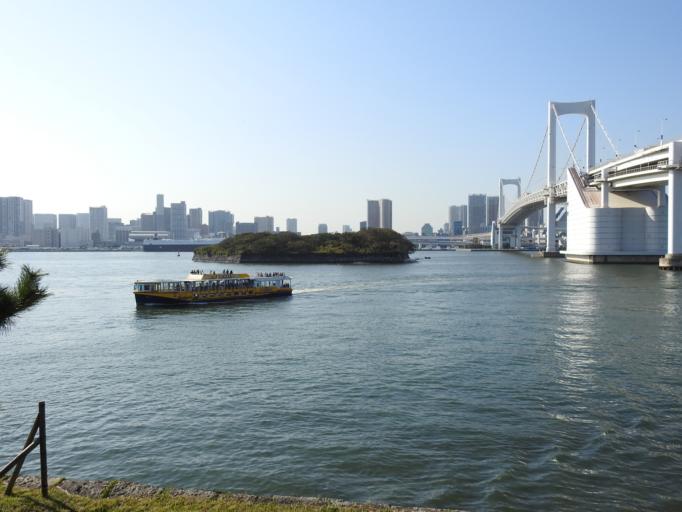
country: JP
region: Tokyo
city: Tokyo
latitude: 35.6332
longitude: 139.7710
